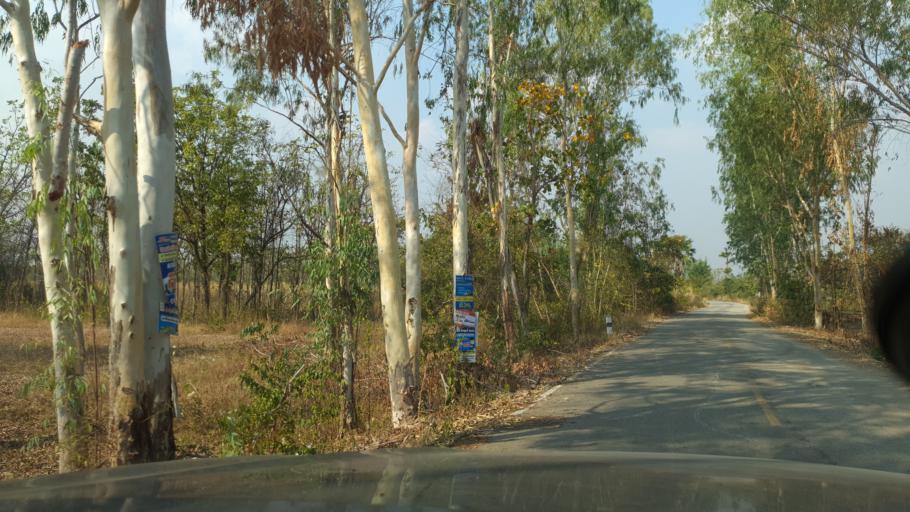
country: TH
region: Sukhothai
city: Ban Dan Lan Hoi
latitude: 17.0096
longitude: 99.5582
